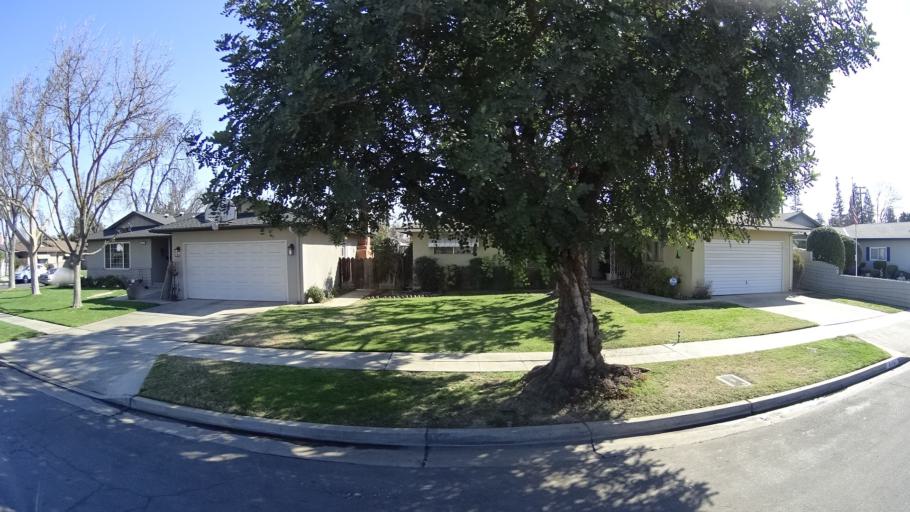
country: US
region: California
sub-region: Fresno County
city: Clovis
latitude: 36.8261
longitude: -119.7763
